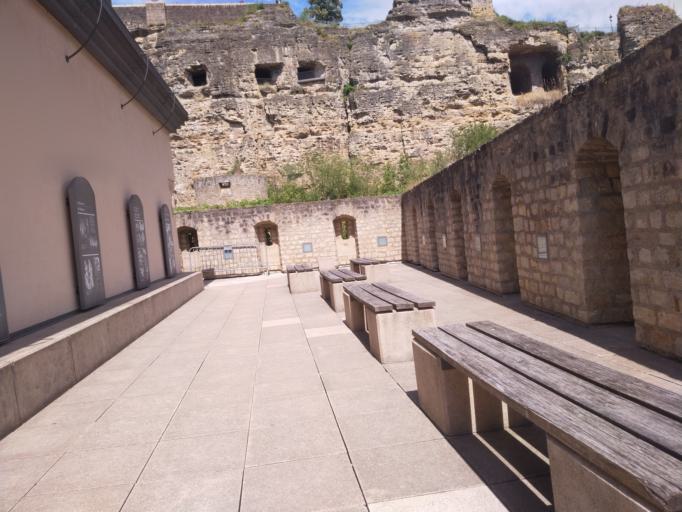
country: LU
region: Luxembourg
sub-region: Canton de Luxembourg
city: Luxembourg
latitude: 49.6110
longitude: 6.1376
